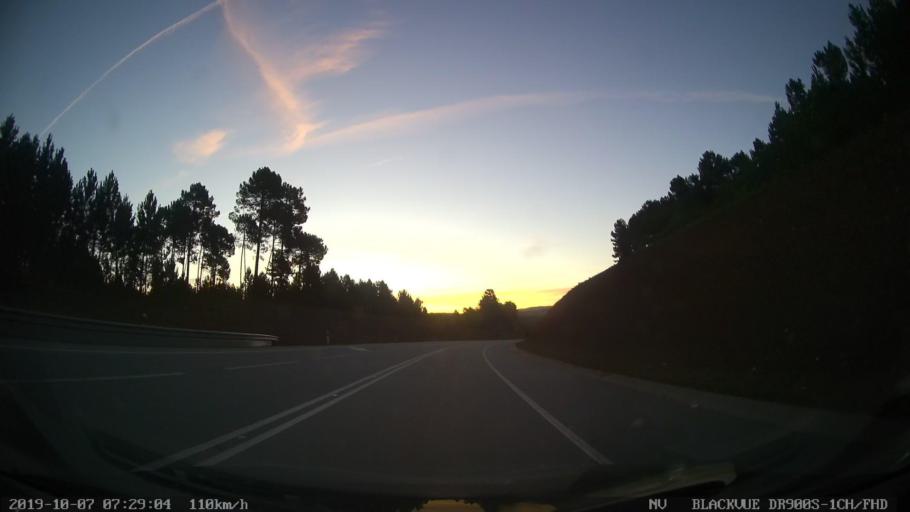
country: PT
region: Vila Real
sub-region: Vila Real
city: Vila Real
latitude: 41.2705
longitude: -7.6801
